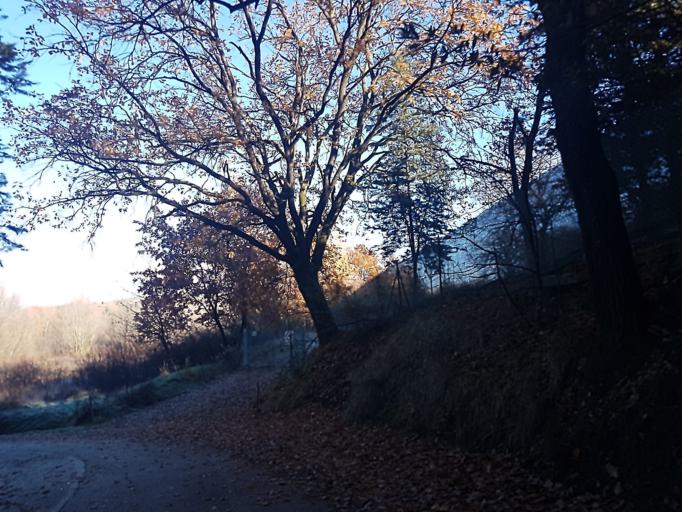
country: IT
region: Umbria
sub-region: Provincia di Perugia
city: Perugia
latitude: 43.0723
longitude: 12.3701
